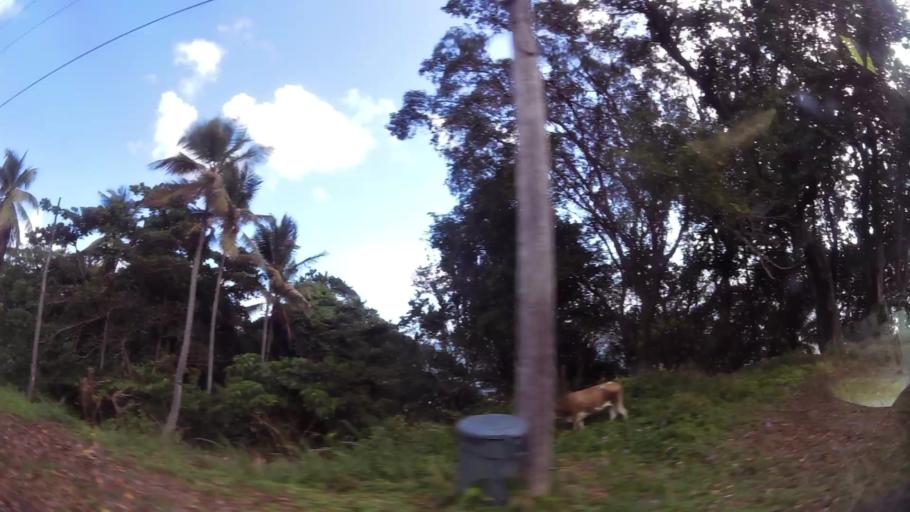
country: DM
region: Saint Andrew
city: Marigot
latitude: 15.5272
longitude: -61.2741
